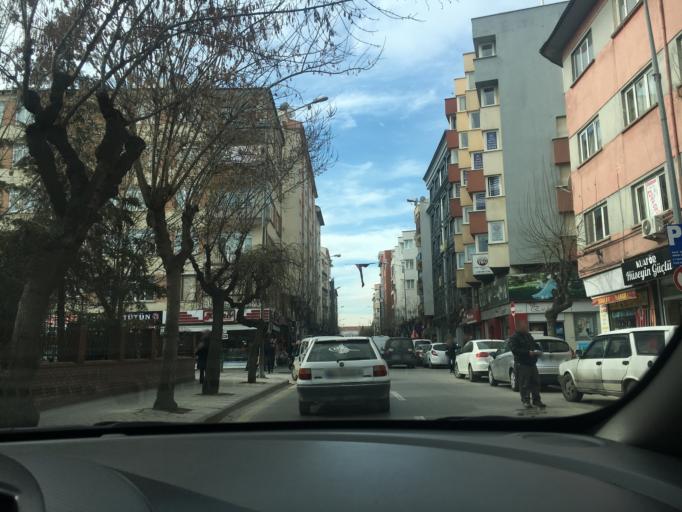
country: TR
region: Eskisehir
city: Eskisehir
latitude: 39.7752
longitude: 30.5155
